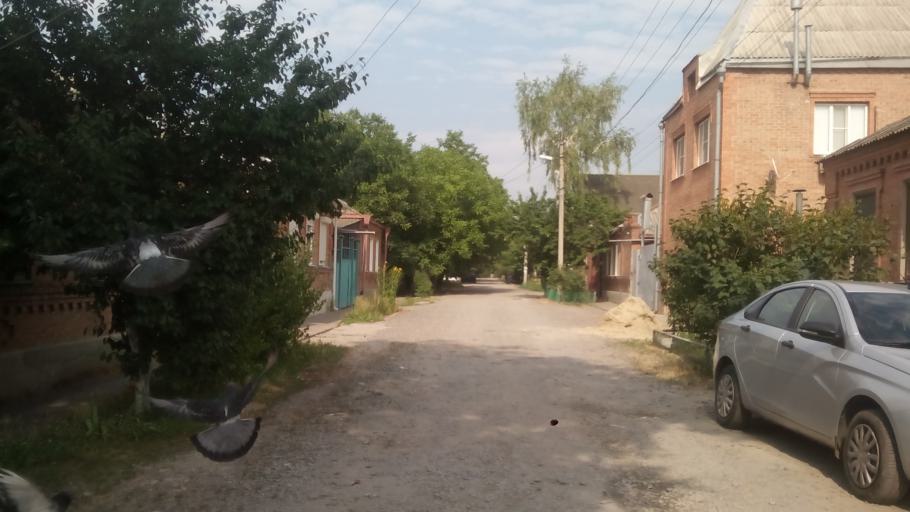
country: RU
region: Rostov
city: Rostov-na-Donu
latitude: 47.2186
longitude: 39.6377
